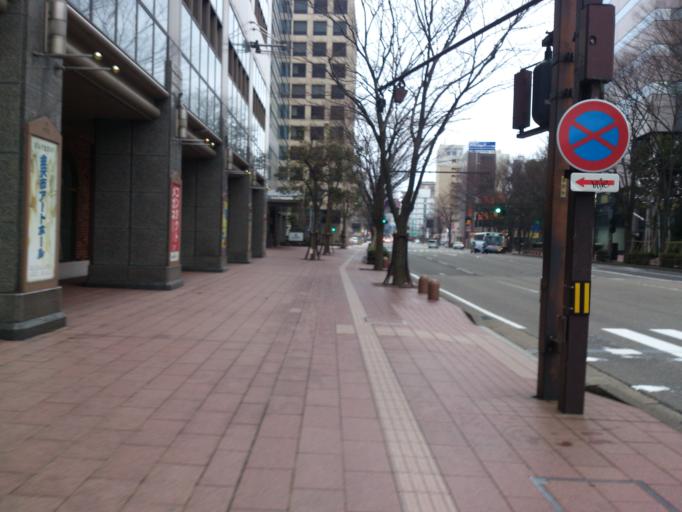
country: JP
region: Ishikawa
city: Kanazawa-shi
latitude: 36.5767
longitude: 136.6494
